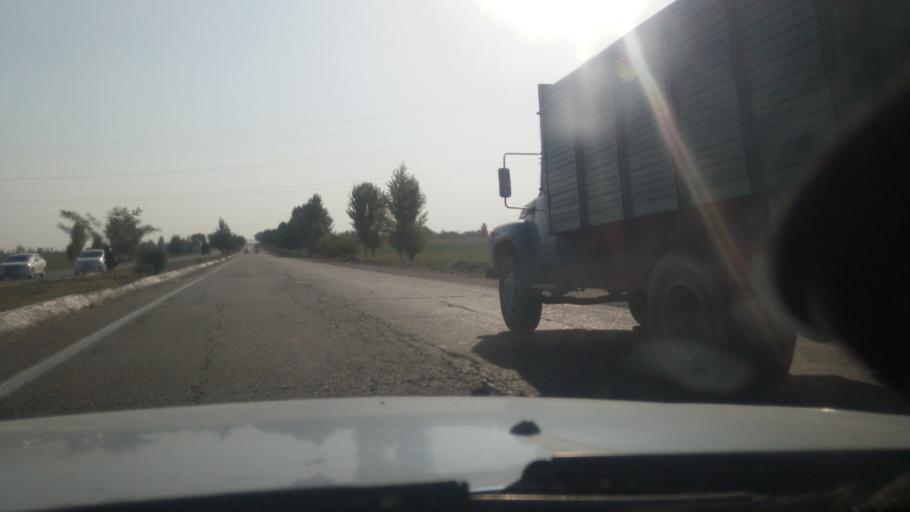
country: UZ
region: Toshkent
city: Zafar
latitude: 41.0221
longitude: 68.8550
